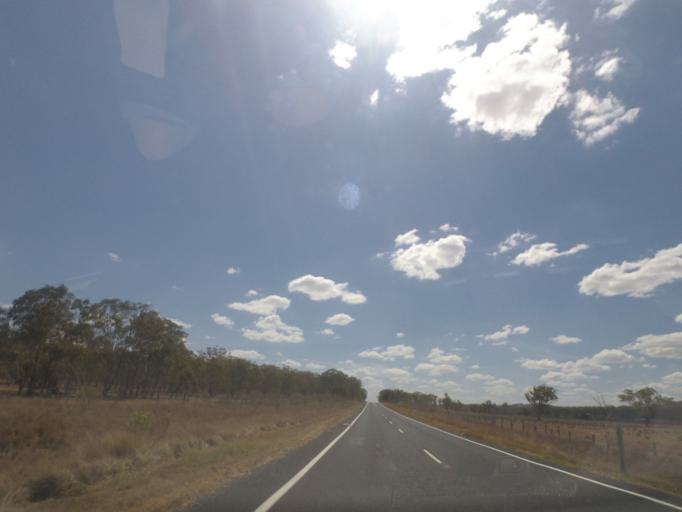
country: AU
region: Queensland
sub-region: Southern Downs
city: Warwick
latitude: -28.1838
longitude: 151.8105
